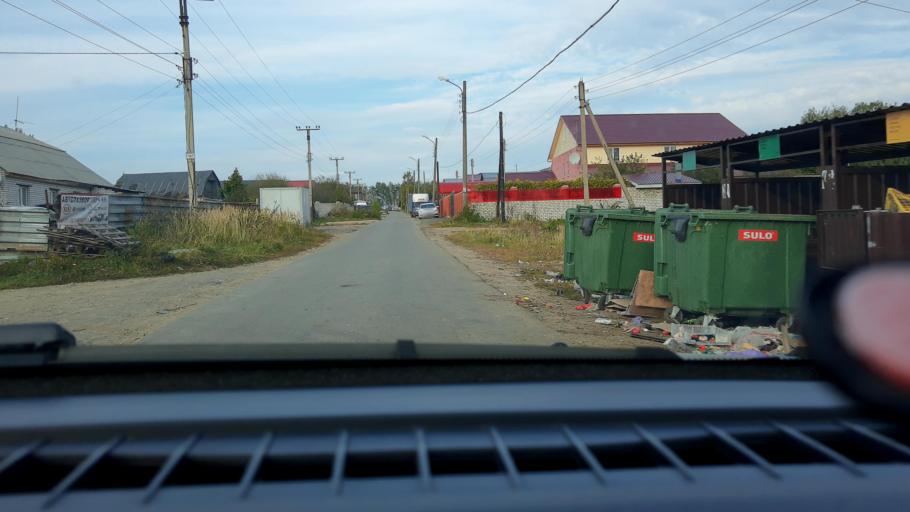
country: RU
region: Nizjnij Novgorod
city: Nizhniy Novgorod
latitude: 56.2112
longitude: 43.9567
